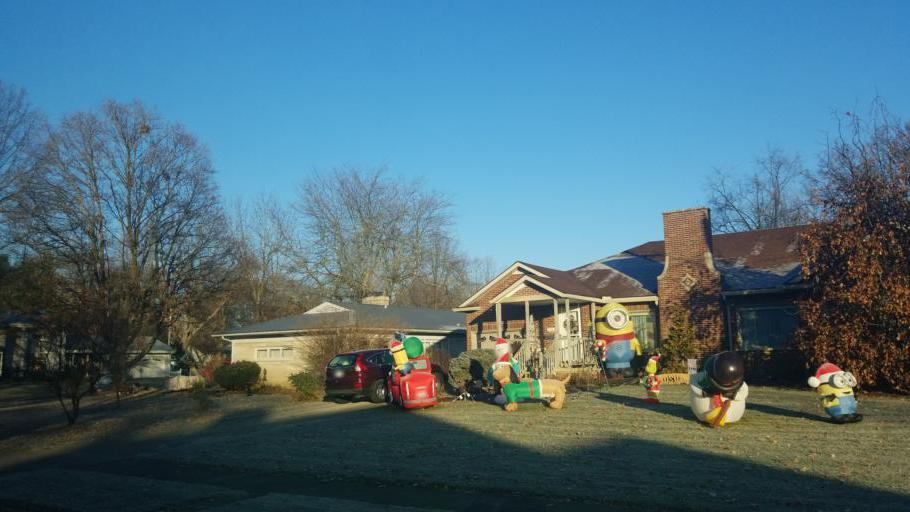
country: US
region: Ohio
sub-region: Marion County
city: Marion
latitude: 40.5783
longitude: -83.1120
